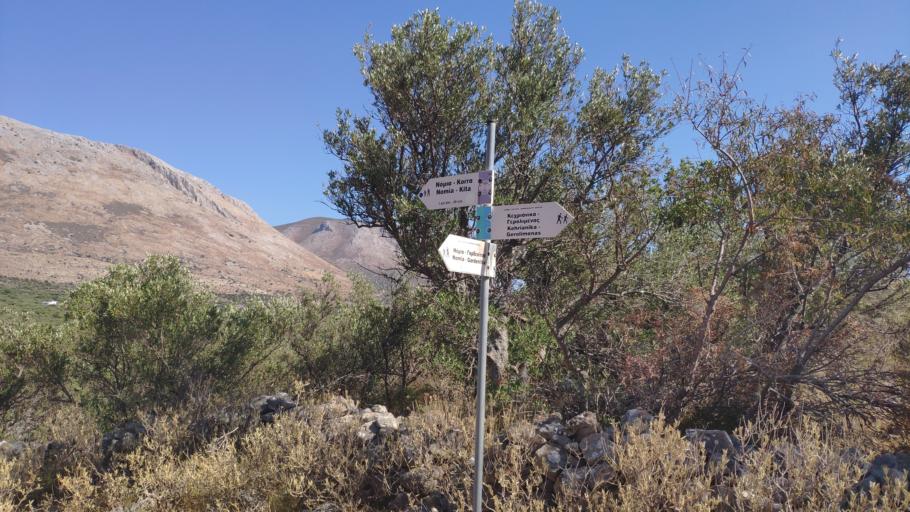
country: GR
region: Peloponnese
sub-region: Nomos Lakonias
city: Gytheio
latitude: 36.5131
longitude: 22.3947
